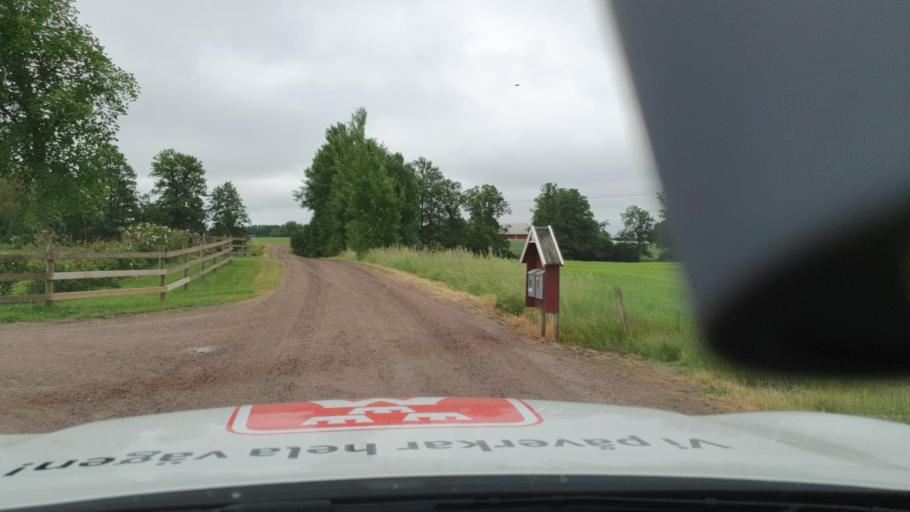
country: SE
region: Vaestra Goetaland
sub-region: Tidaholms Kommun
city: Olofstorp
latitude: 58.3946
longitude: 13.9996
